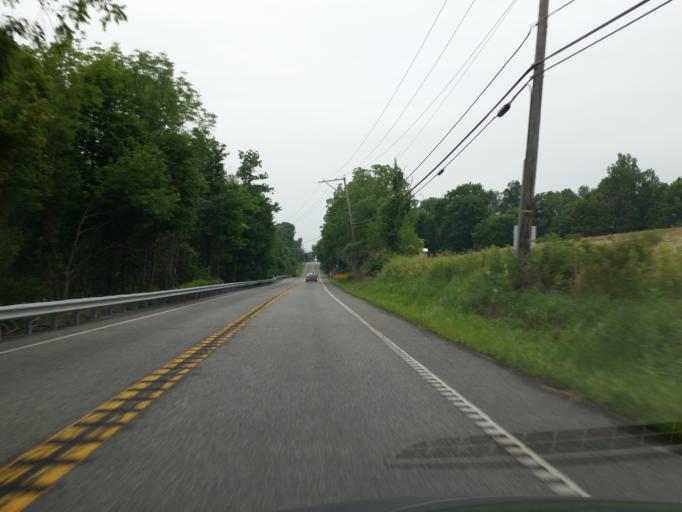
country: US
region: Pennsylvania
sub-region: Lebanon County
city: Jonestown
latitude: 40.4745
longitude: -76.5206
